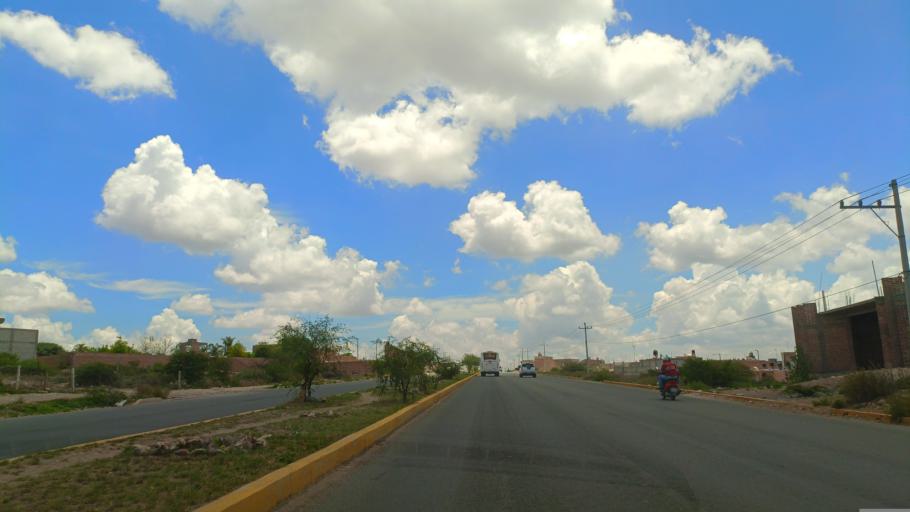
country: MX
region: Guerrero
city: San Luis de la Paz
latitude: 21.2893
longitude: -100.5031
